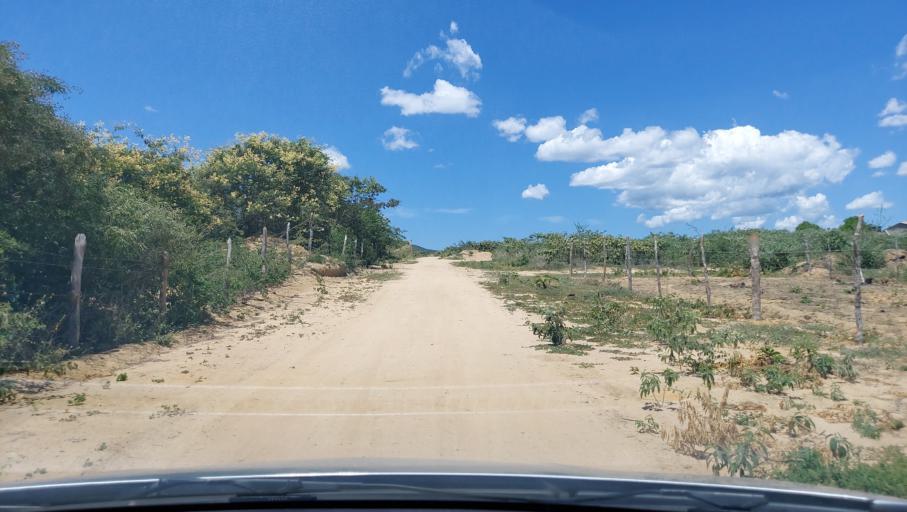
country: BR
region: Bahia
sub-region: Oliveira Dos Brejinhos
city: Beira Rio
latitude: -12.0080
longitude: -42.6327
